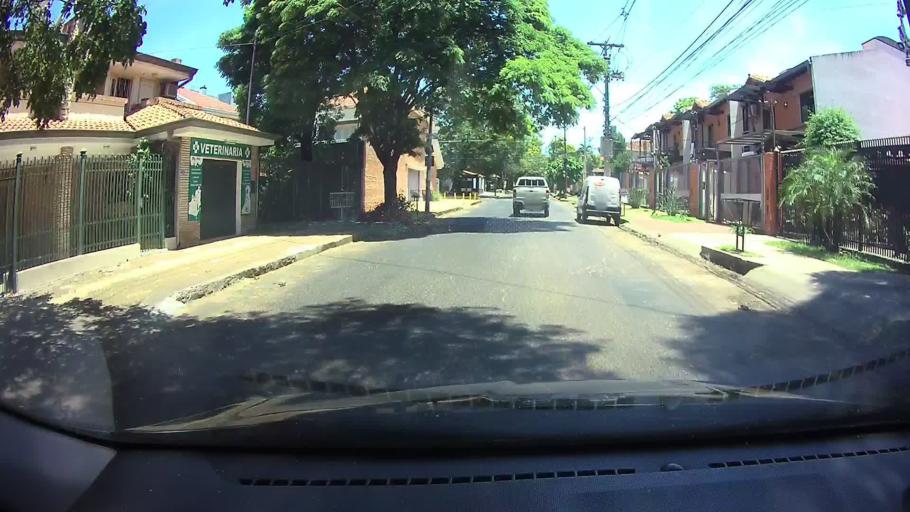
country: PY
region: Asuncion
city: Asuncion
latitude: -25.3001
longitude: -57.5999
